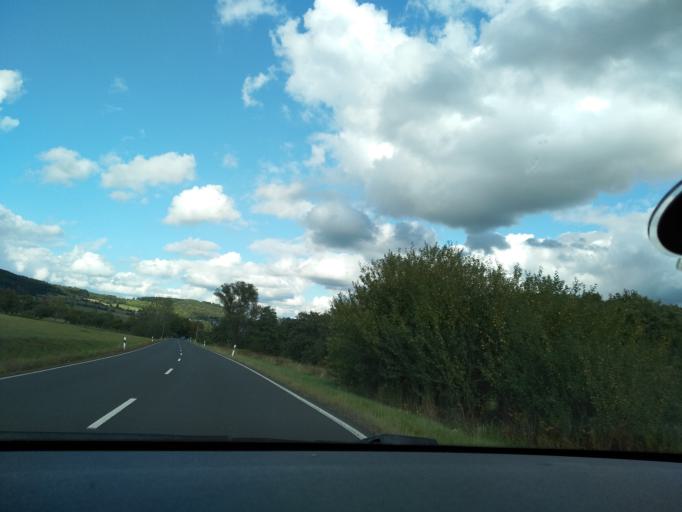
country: DE
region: Hesse
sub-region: Regierungsbezirk Giessen
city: Haiger
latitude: 50.7405
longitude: 8.1540
